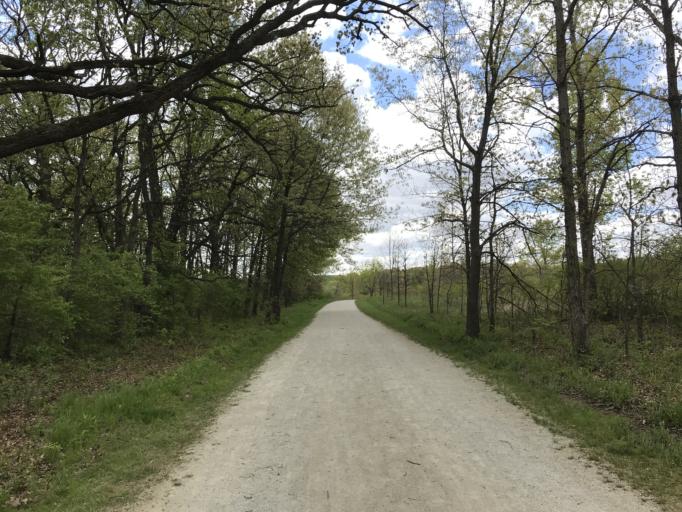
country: US
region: Illinois
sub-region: DuPage County
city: Woodridge
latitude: 41.7381
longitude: -88.0855
